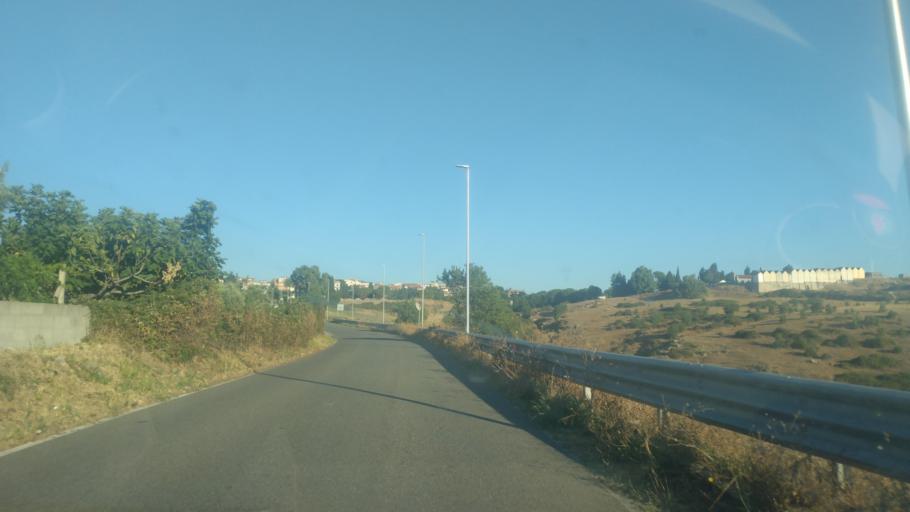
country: IT
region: Calabria
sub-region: Provincia di Catanzaro
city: Staletti
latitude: 38.7649
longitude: 16.5512
